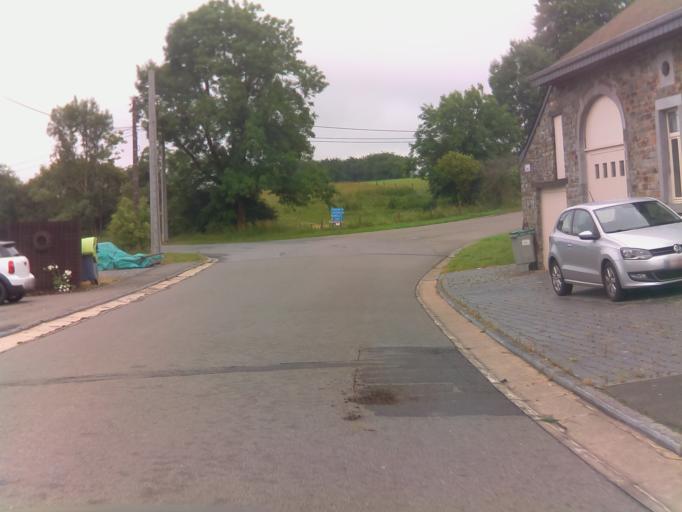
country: BE
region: Wallonia
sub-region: Province du Luxembourg
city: Libin
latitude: 49.9521
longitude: 5.2250
